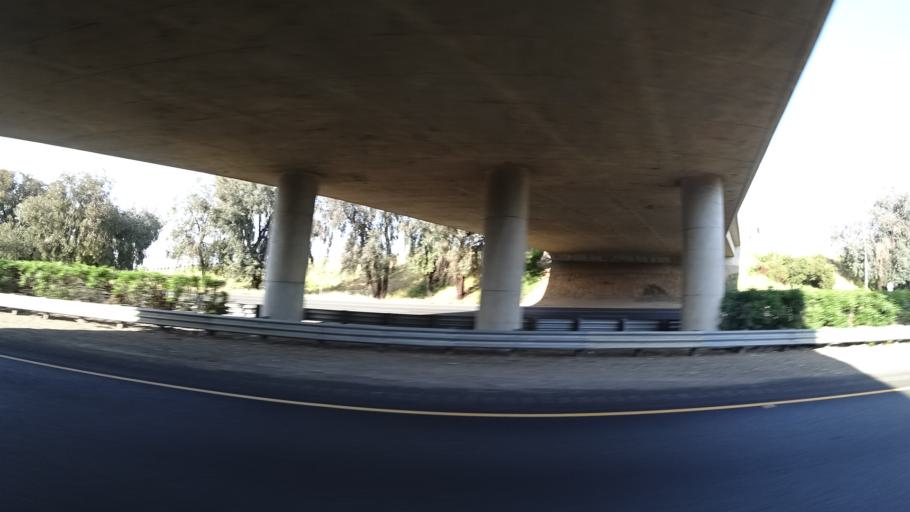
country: US
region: California
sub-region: Yuba County
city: Linda
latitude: 39.1132
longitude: -121.5594
